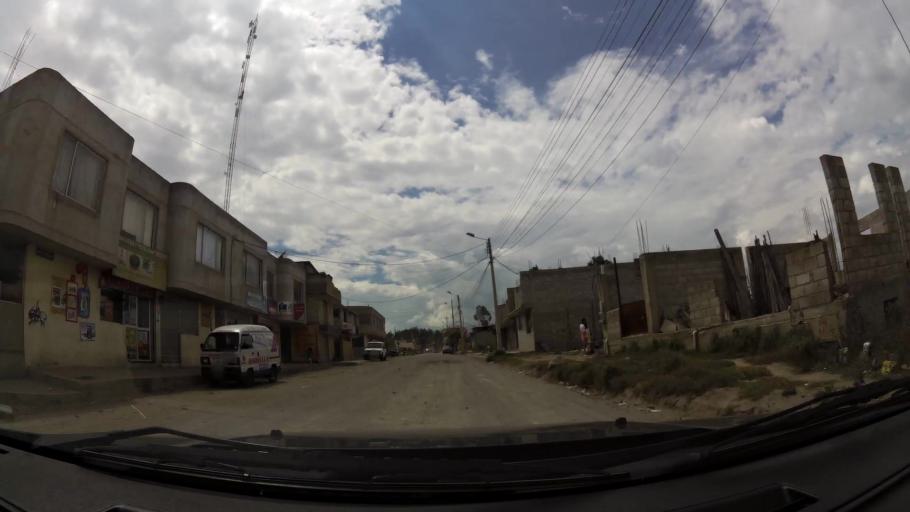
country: EC
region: Pichincha
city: Quito
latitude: -0.0829
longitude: -78.4096
